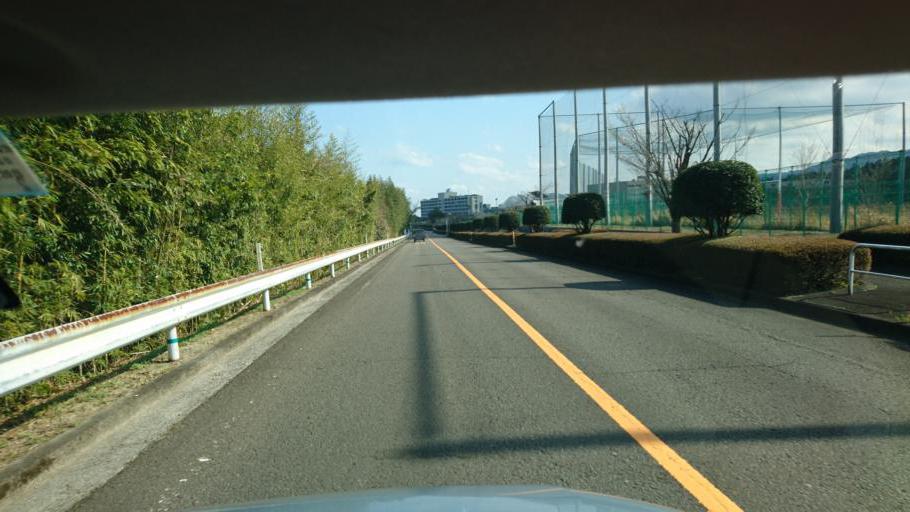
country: JP
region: Miyazaki
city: Miyazaki-shi
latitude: 31.8342
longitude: 131.4082
